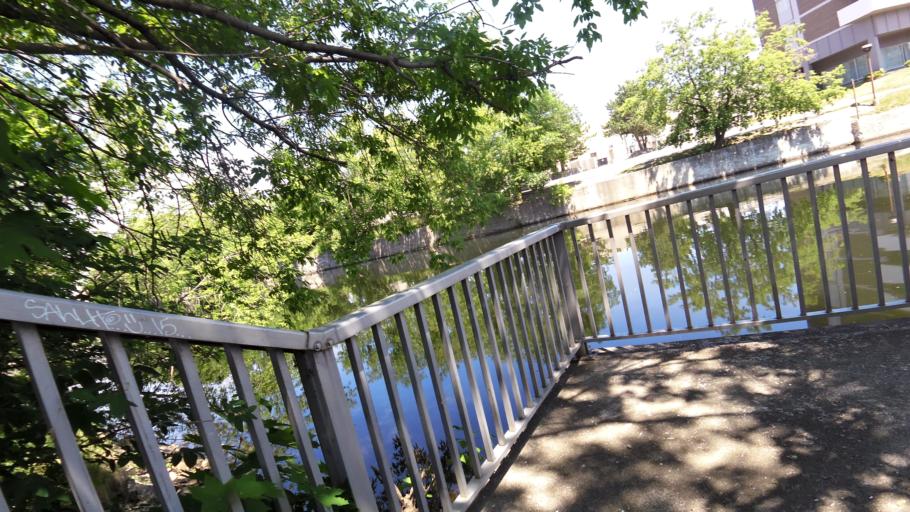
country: CA
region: Ontario
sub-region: Lanark County
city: Smiths Falls
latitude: 44.8974
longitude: -76.0196
